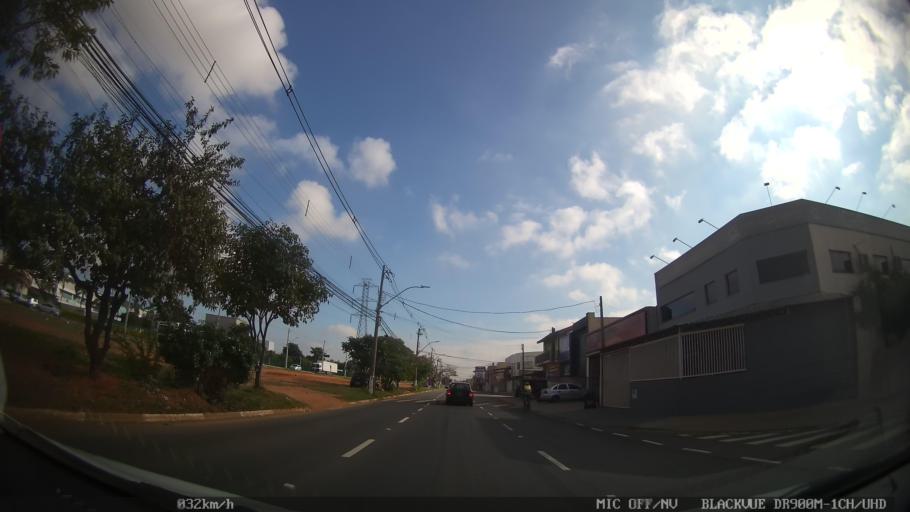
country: BR
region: Sao Paulo
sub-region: Hortolandia
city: Hortolandia
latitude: -22.9015
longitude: -47.1858
